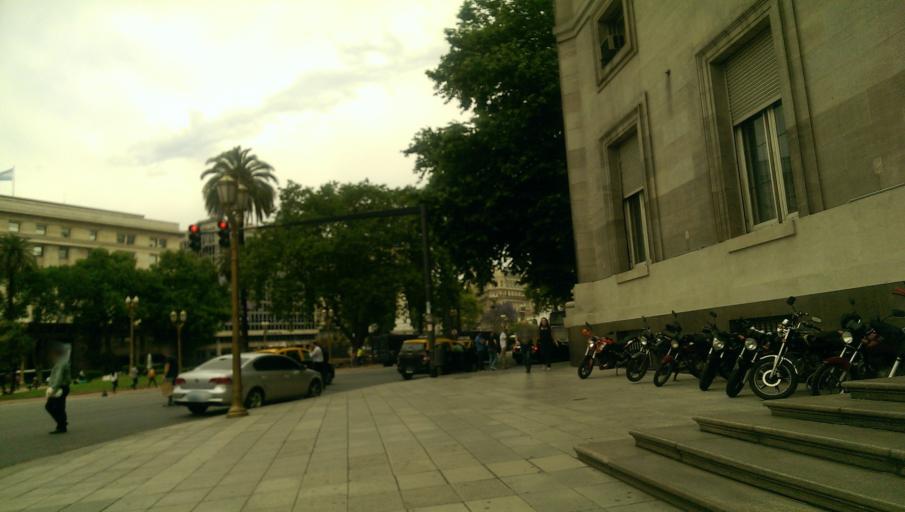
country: AR
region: Buenos Aires F.D.
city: Buenos Aires
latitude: -34.6077
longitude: -58.3711
